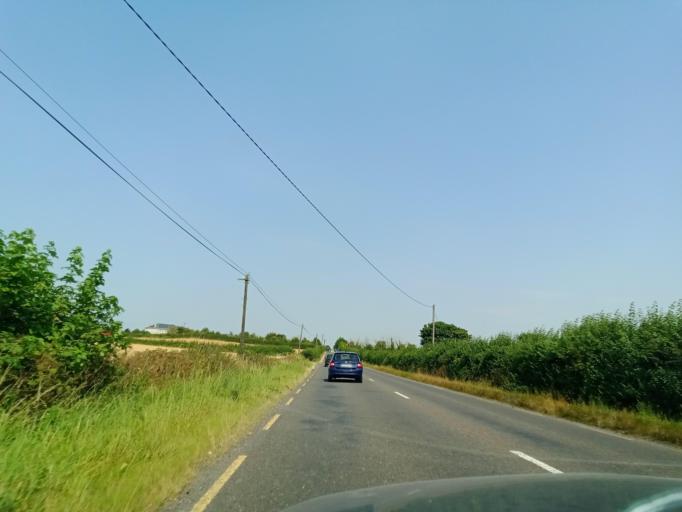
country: IE
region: Leinster
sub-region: Laois
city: Portlaoise
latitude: 53.0555
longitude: -7.2371
